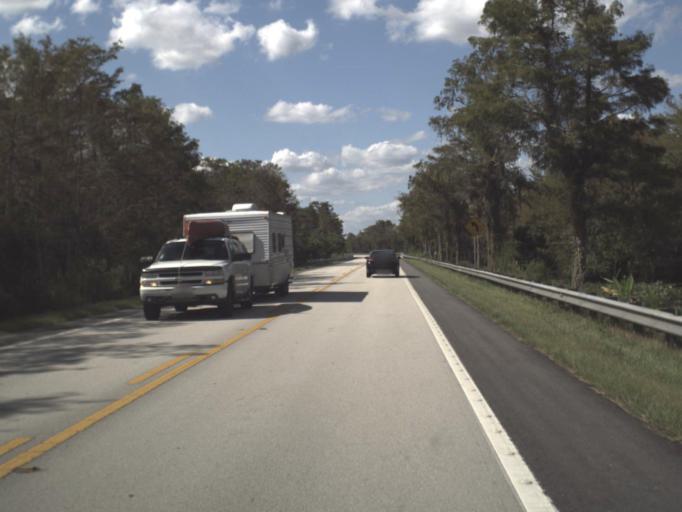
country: US
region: Florida
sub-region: Miami-Dade County
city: Kendall West
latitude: 25.8423
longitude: -80.9160
